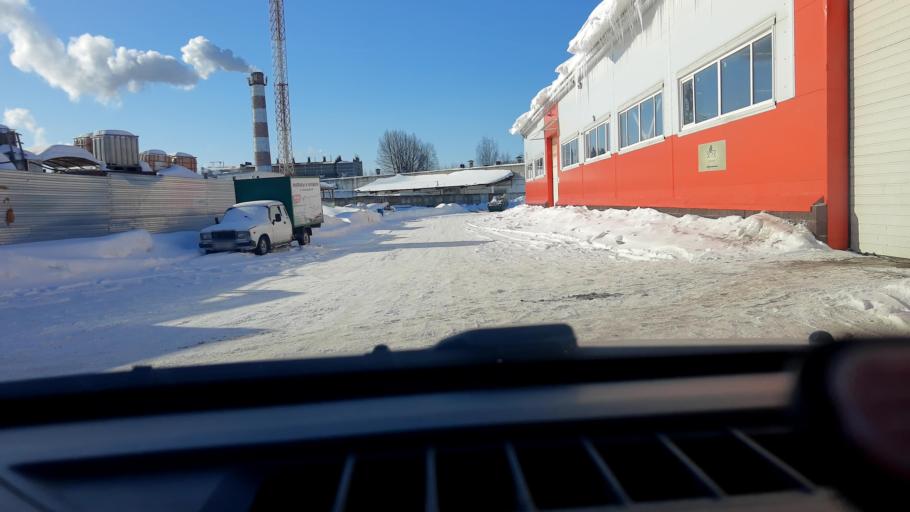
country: RU
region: Nizjnij Novgorod
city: Gorbatovka
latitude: 56.3471
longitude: 43.8175
